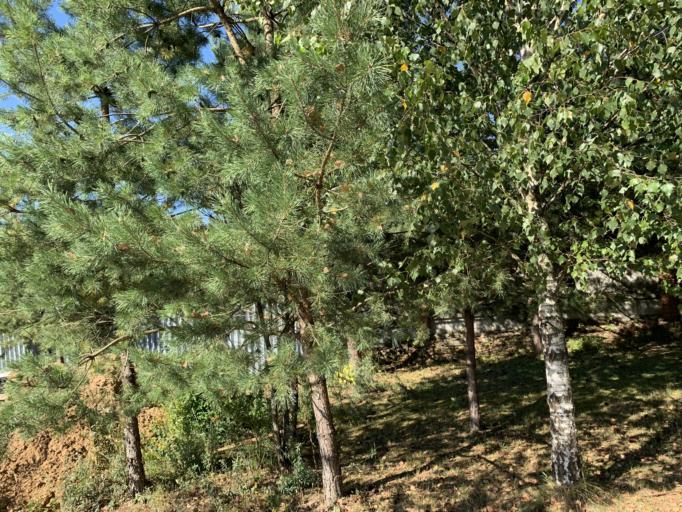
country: RU
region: Moskovskaya
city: Mamontovka
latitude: 55.9693
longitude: 37.8362
